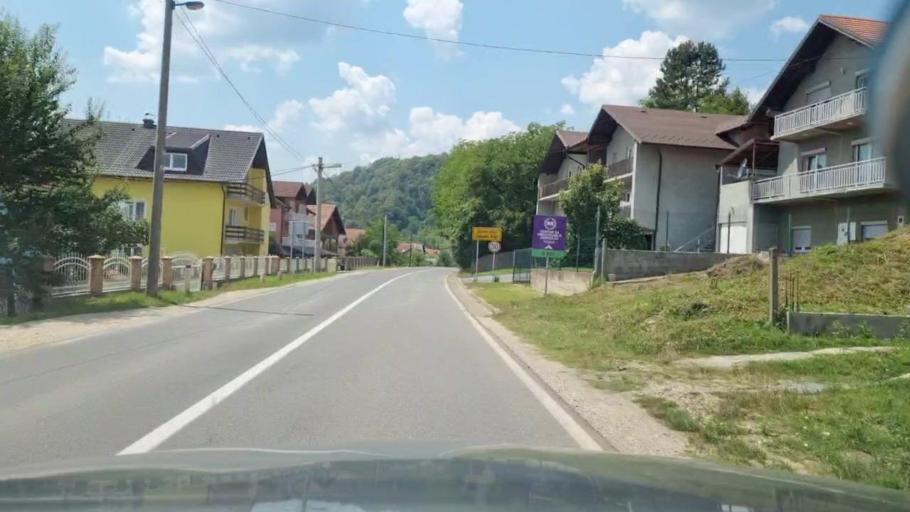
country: BA
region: Federation of Bosnia and Herzegovina
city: Gornja Tuzla
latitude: 44.5306
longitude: 18.7522
